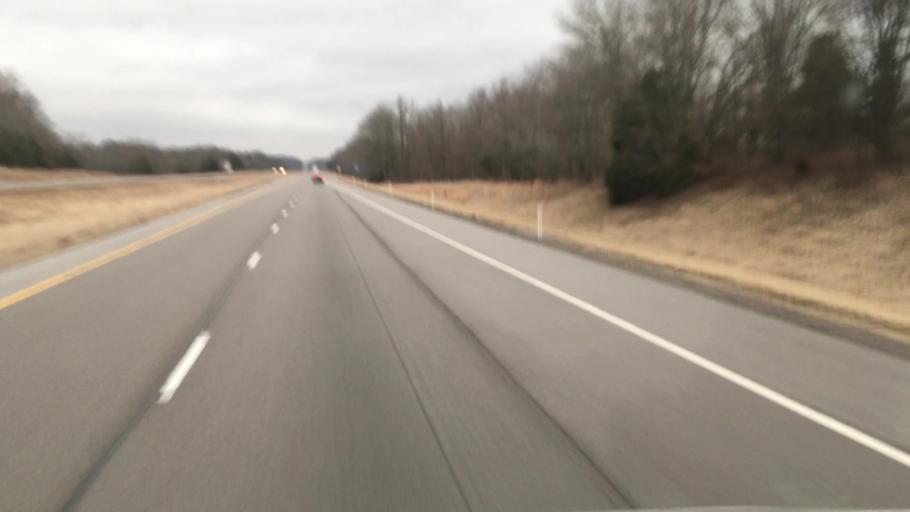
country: US
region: Illinois
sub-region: Johnson County
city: Vienna
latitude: 37.4523
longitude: -88.8879
